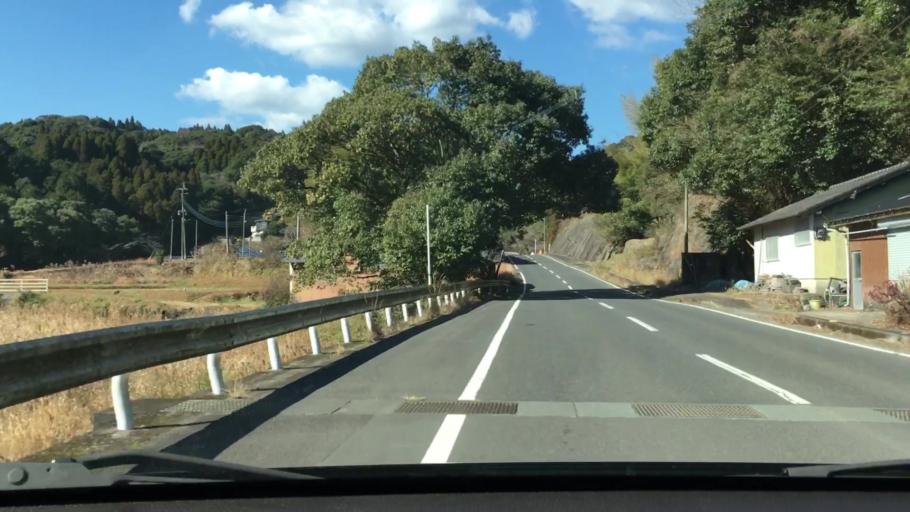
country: JP
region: Kagoshima
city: Ijuin
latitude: 31.6990
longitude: 130.4592
